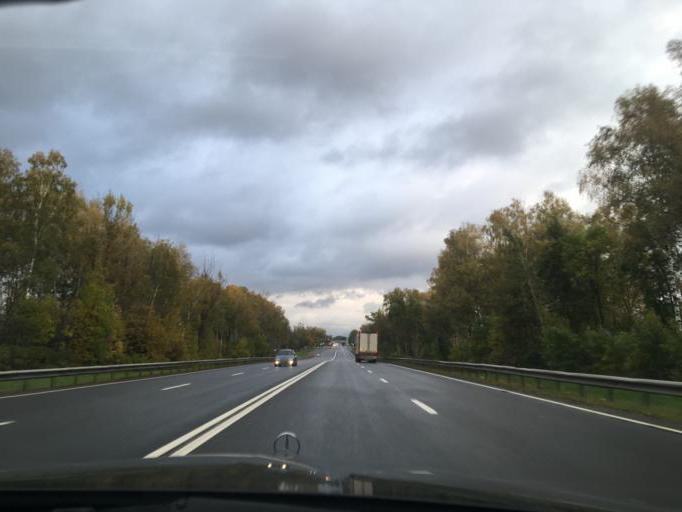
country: RU
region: Smolensk
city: Pechersk
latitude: 54.8626
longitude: 31.9488
